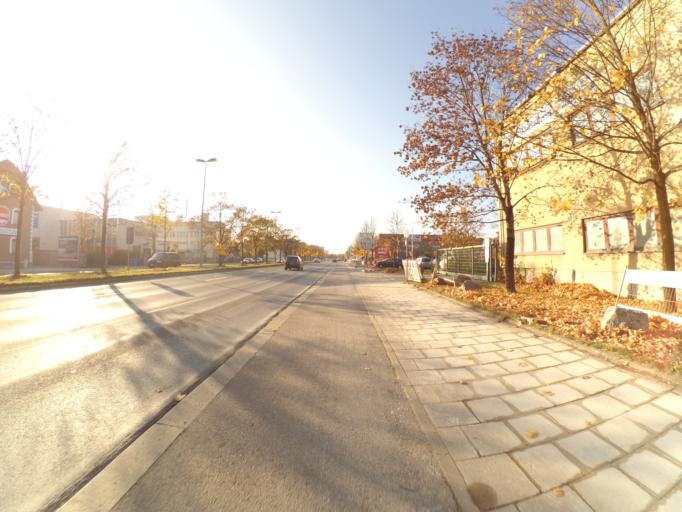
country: DE
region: Bavaria
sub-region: Upper Bavaria
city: Munich
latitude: 48.1869
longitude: 11.5374
